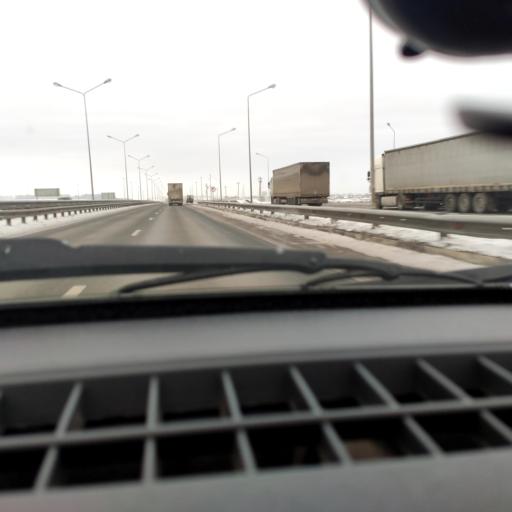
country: RU
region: Bashkortostan
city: Kushnarenkovo
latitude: 55.0733
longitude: 55.2879
